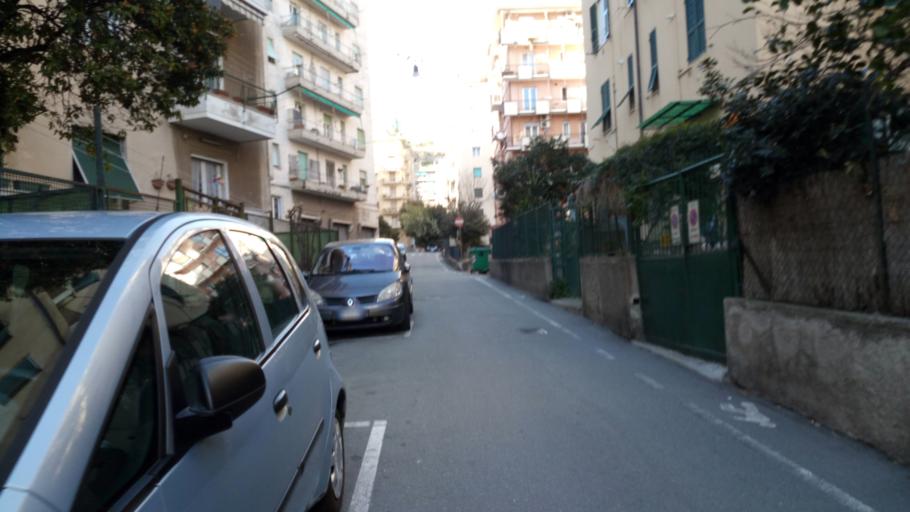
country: IT
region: Liguria
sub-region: Provincia di Genova
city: Mele
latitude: 44.4285
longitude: 8.7727
